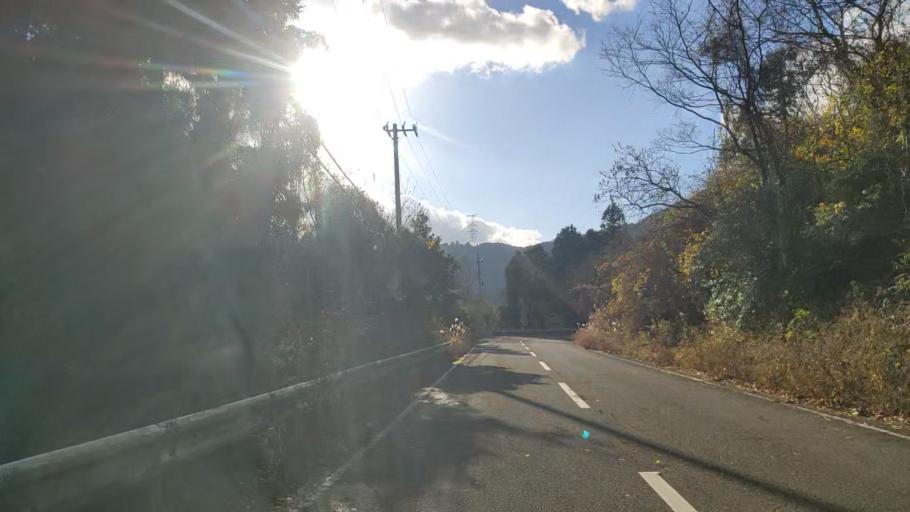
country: JP
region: Ehime
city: Saijo
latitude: 33.8796
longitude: 133.1710
